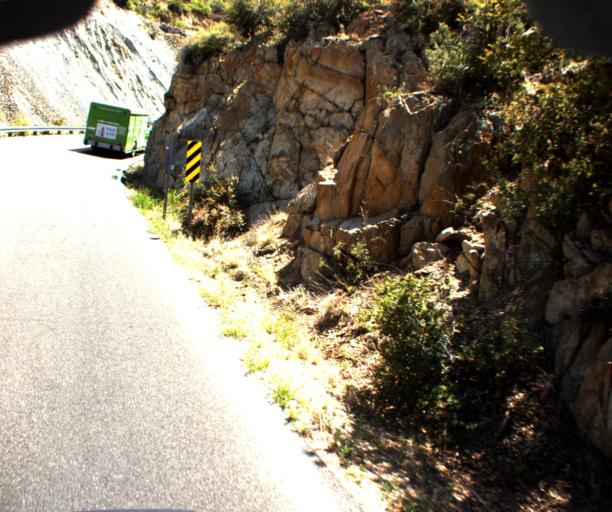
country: US
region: Arizona
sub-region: Yavapai County
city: Clarkdale
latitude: 34.7419
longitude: -112.1215
